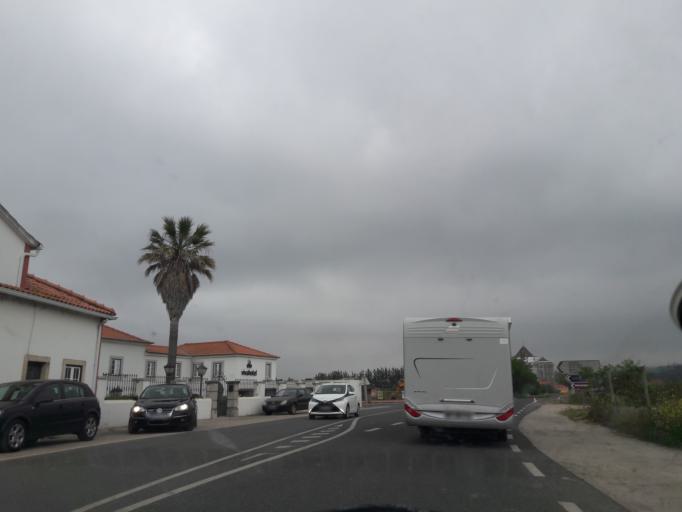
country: PT
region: Leiria
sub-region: Obidos
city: Obidos
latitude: 39.3617
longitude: -9.1544
